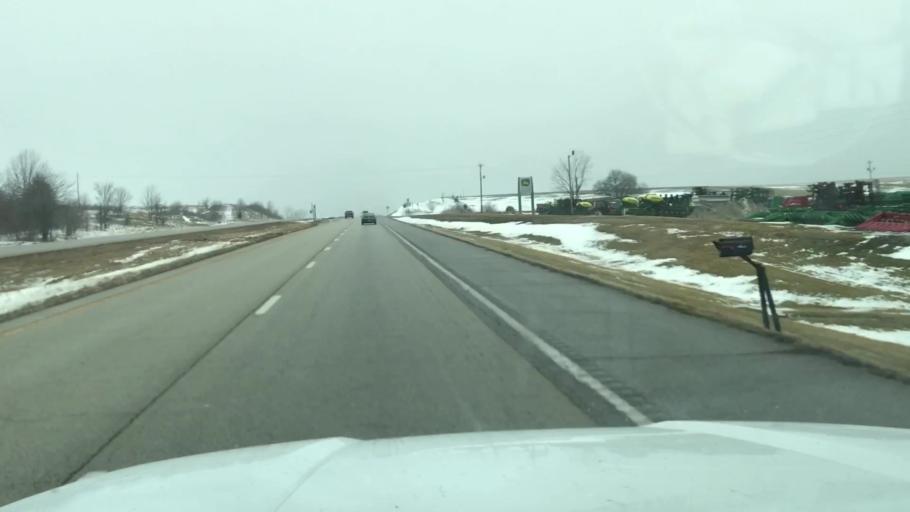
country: US
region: Missouri
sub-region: Clinton County
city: Gower
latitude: 39.7477
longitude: -94.6804
